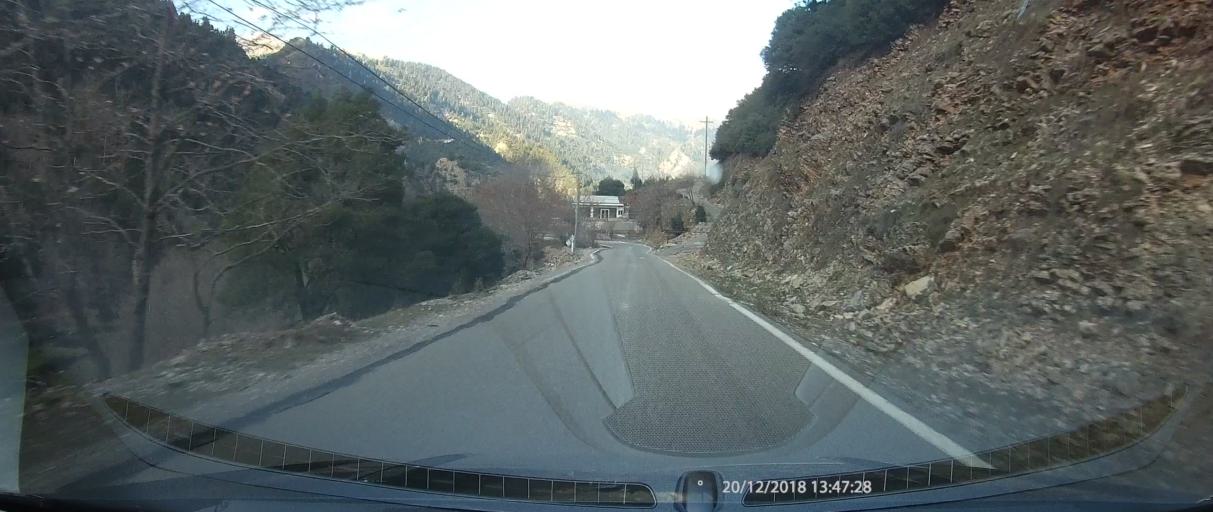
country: GR
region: West Greece
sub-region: Nomos Aitolias kai Akarnanias
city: Thermo
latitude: 38.6815
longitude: 21.6138
